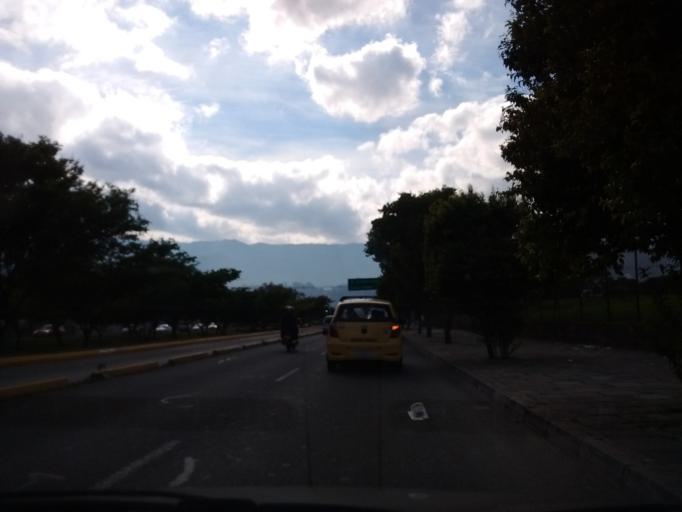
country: CO
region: Antioquia
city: Medellin
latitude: 6.2315
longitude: -75.5884
